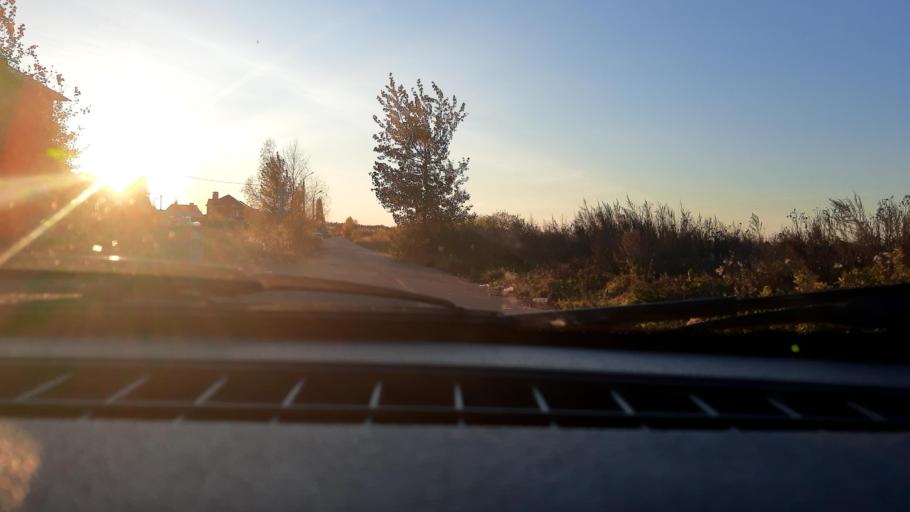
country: RU
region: Bashkortostan
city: Ufa
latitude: 54.8587
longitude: 56.0224
